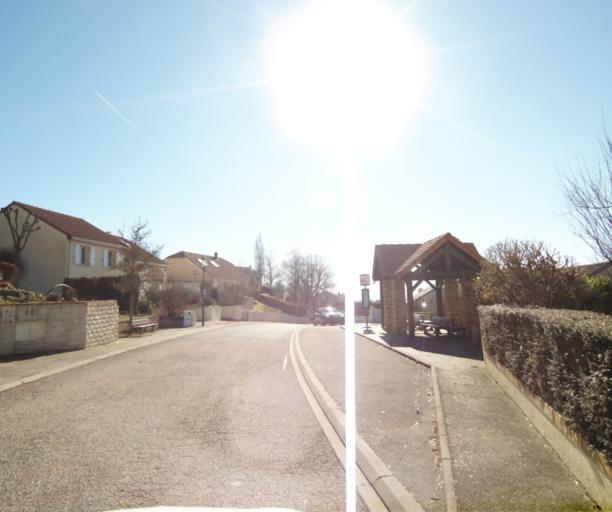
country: FR
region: Lorraine
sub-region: Departement de Meurthe-et-Moselle
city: Essey-les-Nancy
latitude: 48.7157
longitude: 6.2213
